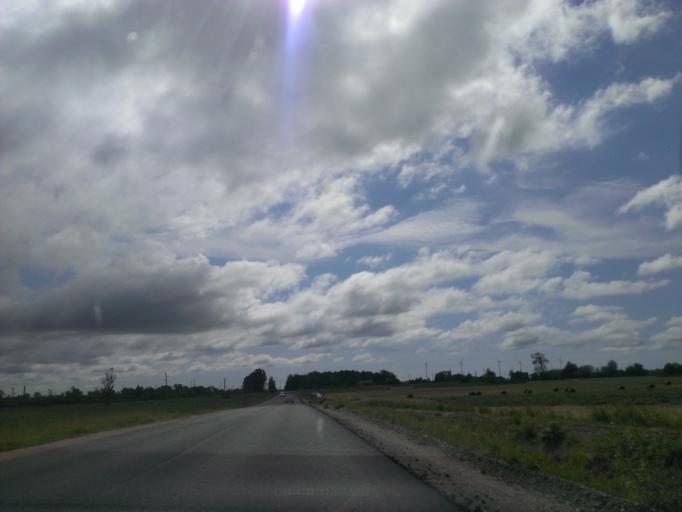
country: LV
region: Durbe
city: Liegi
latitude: 56.5695
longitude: 21.2790
